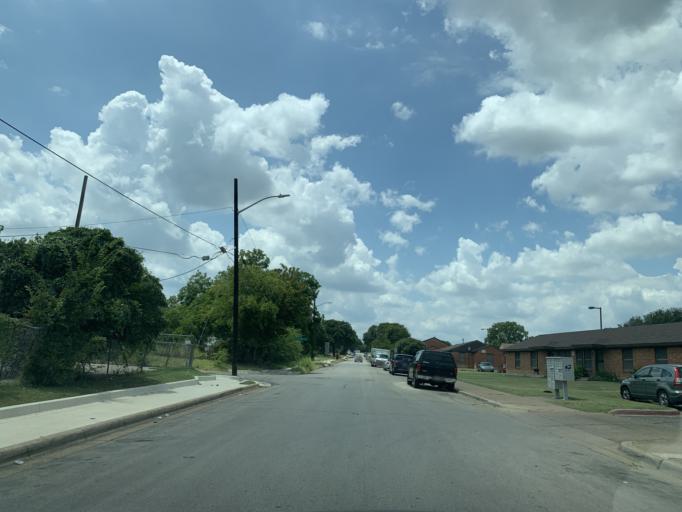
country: US
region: Texas
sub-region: Tarrant County
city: Forest Hill
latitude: 32.7286
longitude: -97.2458
